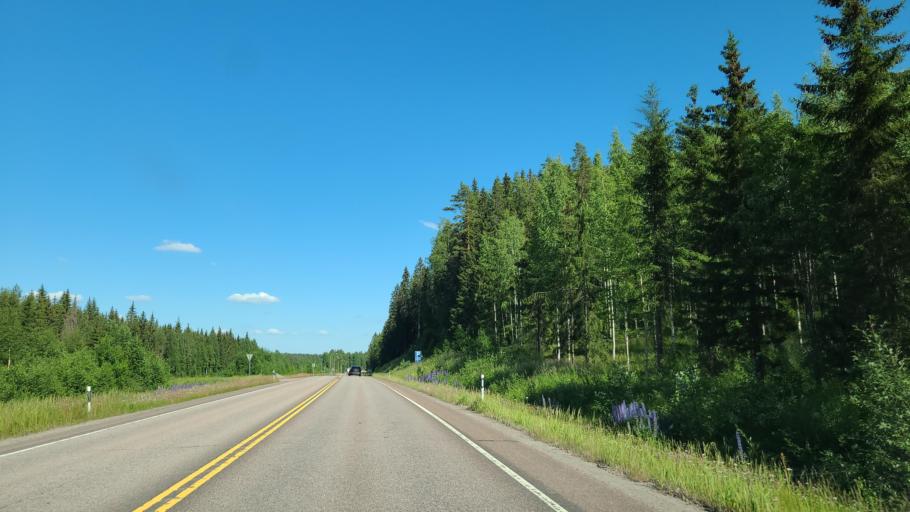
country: FI
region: Central Finland
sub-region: Jyvaeskylae
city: Petaejaevesi
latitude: 62.2713
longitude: 25.3794
